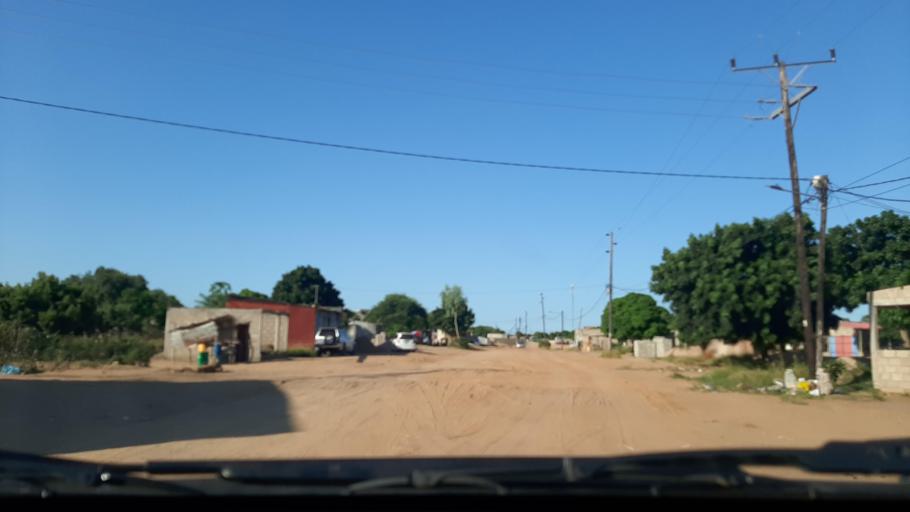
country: MZ
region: Maputo City
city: Maputo
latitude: -25.8011
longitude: 32.5490
